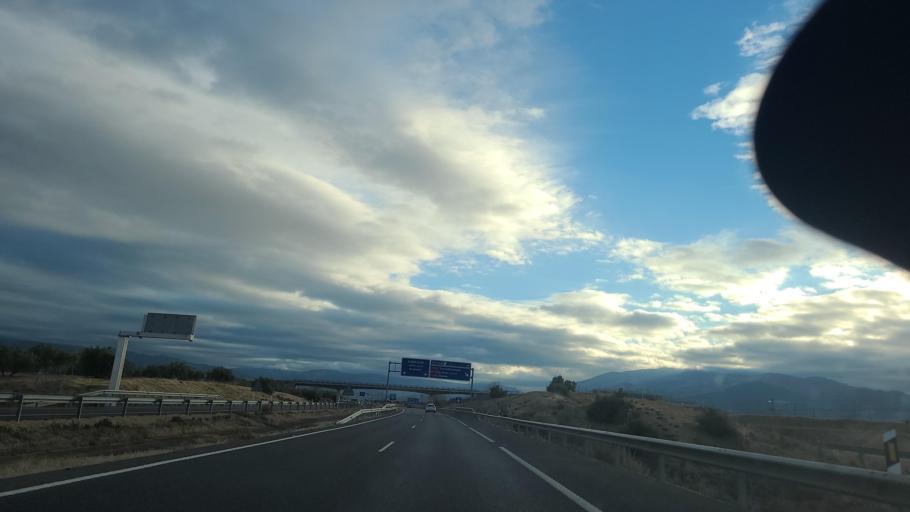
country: ES
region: Andalusia
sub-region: Provincia de Jaen
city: Jaen
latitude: 37.8312
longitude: -3.7664
